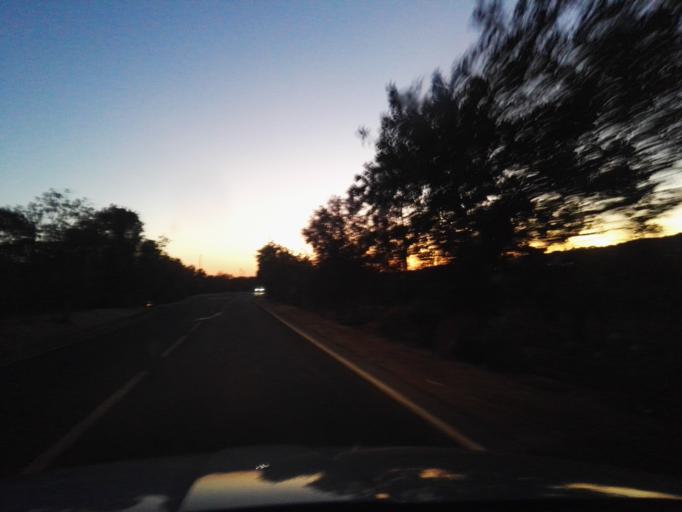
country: PT
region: Faro
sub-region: Faro
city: Santa Barbara de Nexe
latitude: 37.1502
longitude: -7.9447
